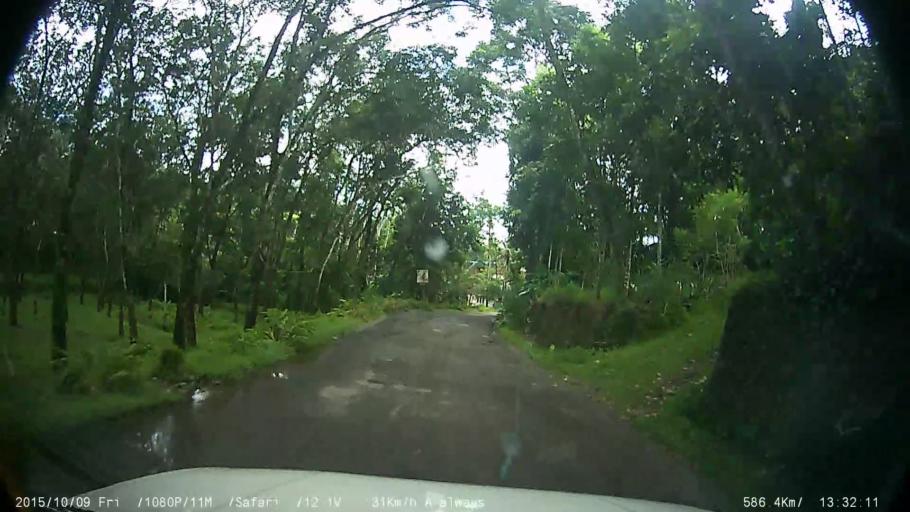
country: IN
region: Kerala
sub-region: Ernakulam
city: Ramamangalam
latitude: 9.9118
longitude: 76.5579
